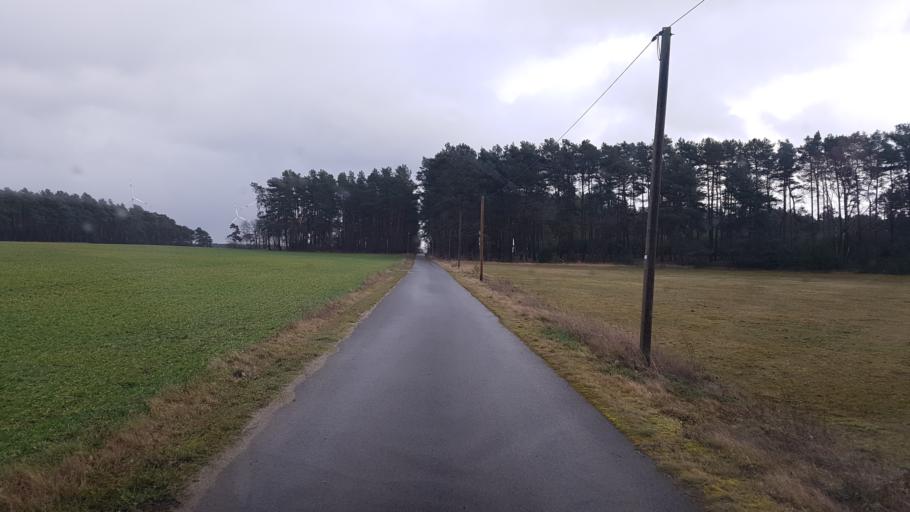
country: DE
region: Brandenburg
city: Sallgast
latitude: 51.6529
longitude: 13.8496
